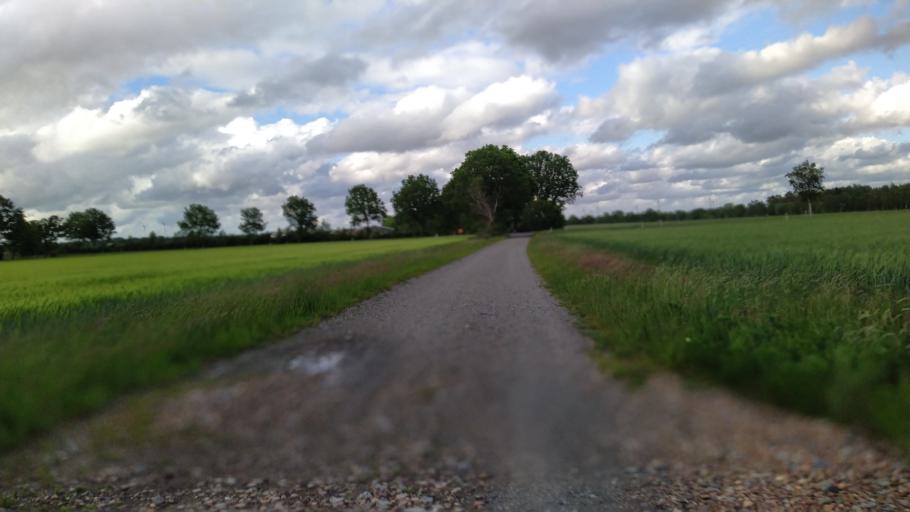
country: DE
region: Lower Saxony
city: Farven
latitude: 53.4586
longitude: 9.3073
